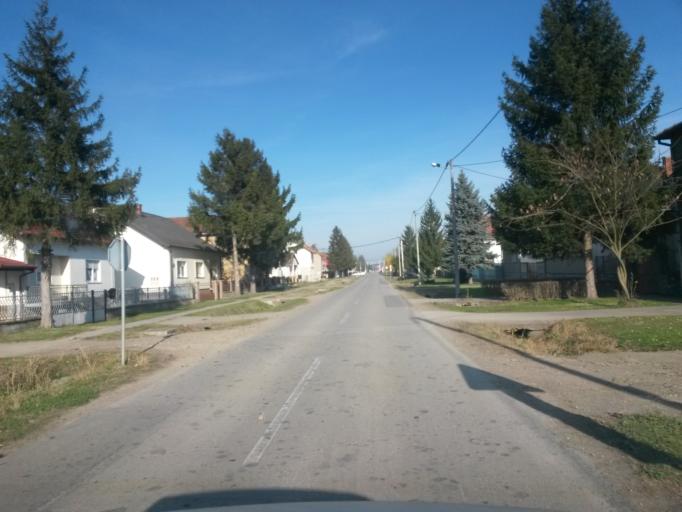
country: HR
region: Vukovarsko-Srijemska
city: Slakovci
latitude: 45.2440
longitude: 18.8997
